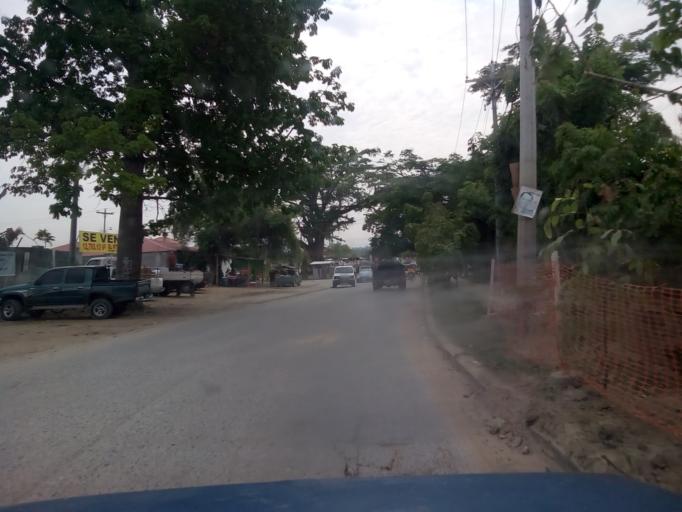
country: HN
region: Cortes
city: San Pedro Sula
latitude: 15.4993
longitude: -87.9862
